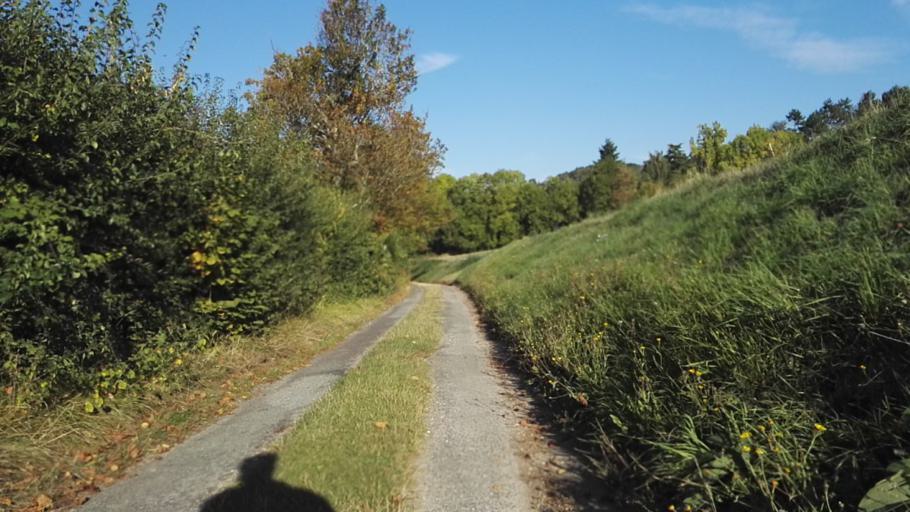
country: FR
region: Haute-Normandie
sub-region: Departement de l'Eure
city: Houlbec-Cocherel
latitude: 49.0550
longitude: 1.3374
